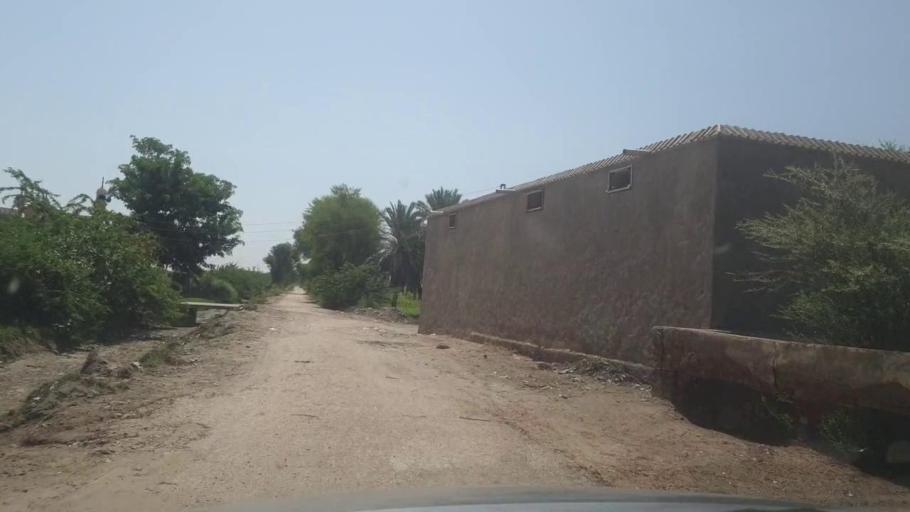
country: PK
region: Sindh
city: Khairpur
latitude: 27.3630
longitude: 69.0281
